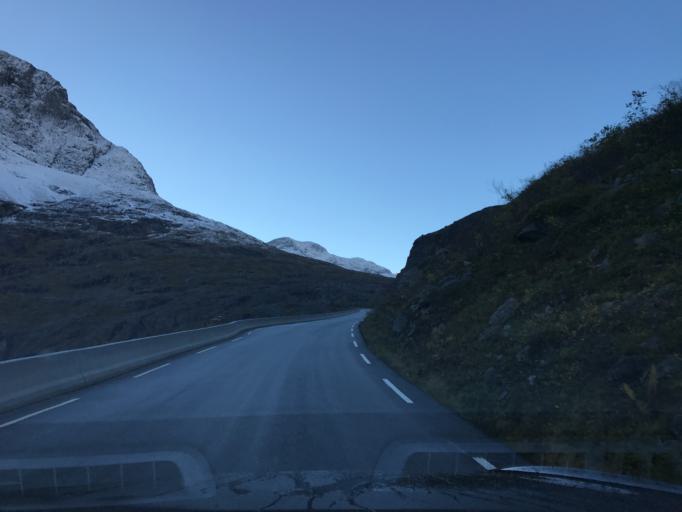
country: NO
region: More og Romsdal
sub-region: Rauma
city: Andalsnes
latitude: 62.4620
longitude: 7.6657
